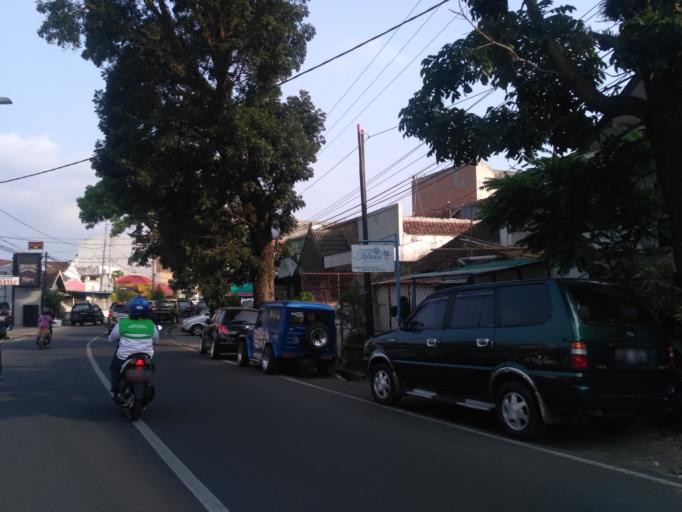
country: ID
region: East Java
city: Malang
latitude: -7.9665
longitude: 112.6287
